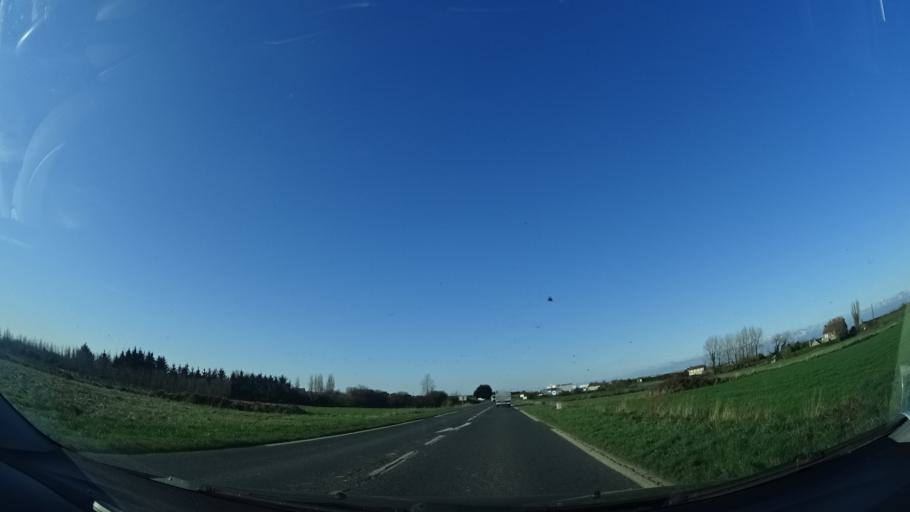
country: FR
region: Brittany
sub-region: Departement du Finistere
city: Saint-Pol-de-Leon
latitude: 48.6641
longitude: -3.9921
